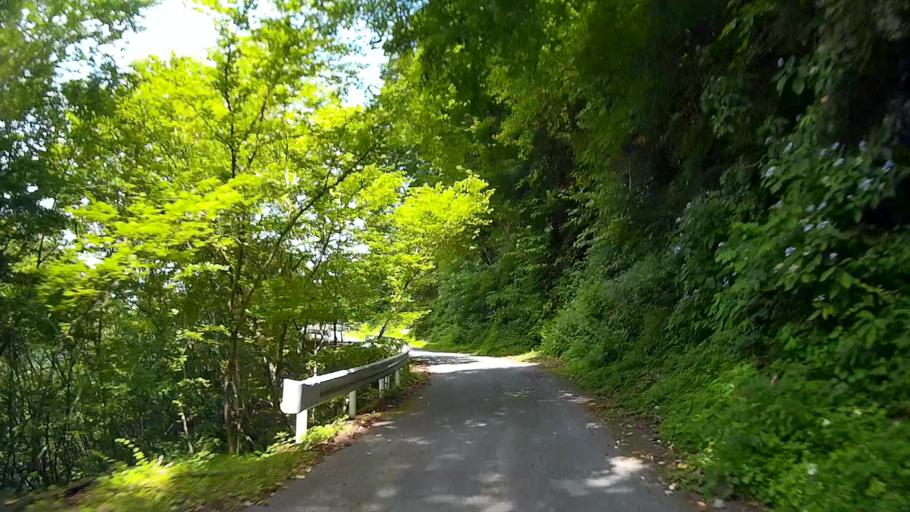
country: JP
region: Saitama
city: Chichibu
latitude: 35.8879
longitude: 139.0995
